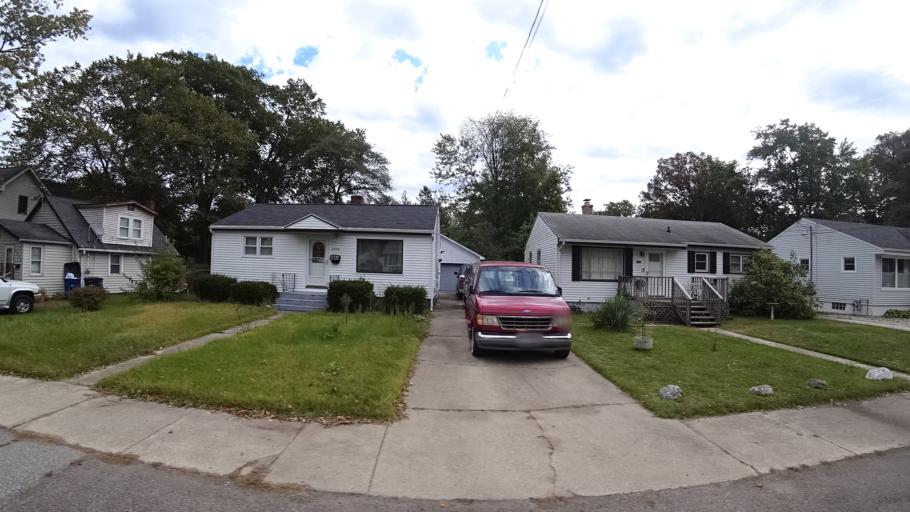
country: US
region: Indiana
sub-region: LaPorte County
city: Michigan City
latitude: 41.6971
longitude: -86.8802
